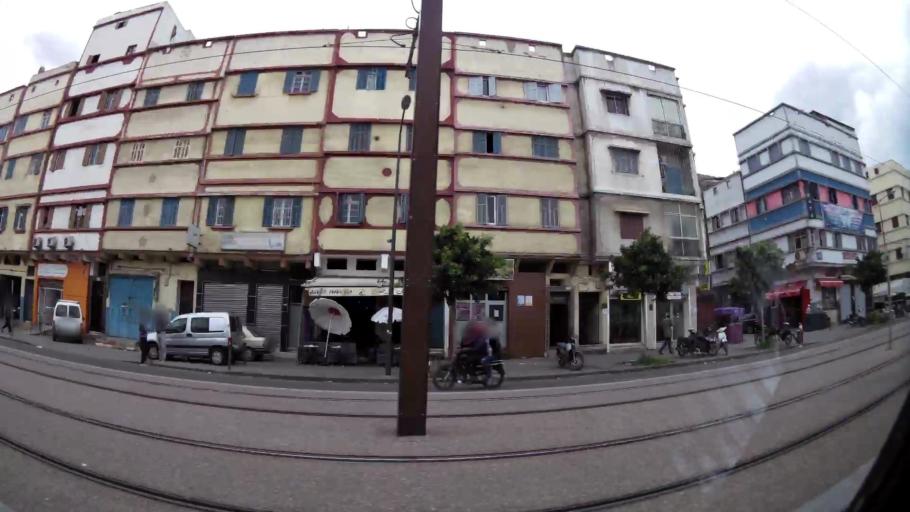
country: MA
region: Grand Casablanca
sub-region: Casablanca
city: Casablanca
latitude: 33.5872
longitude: -7.5673
